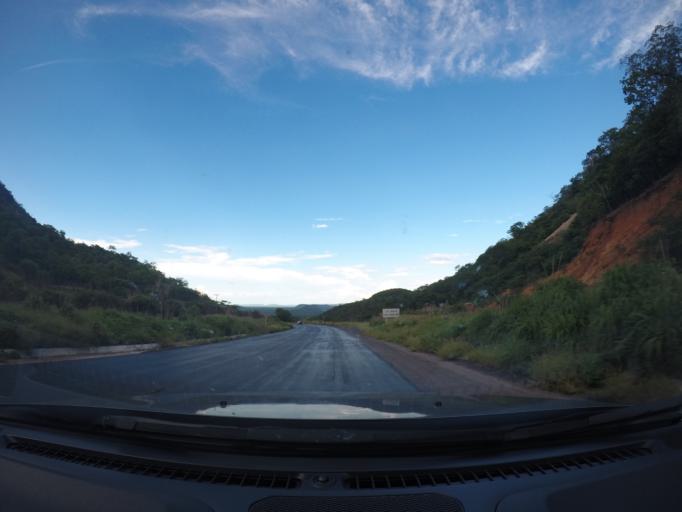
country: BR
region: Bahia
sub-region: Ibotirama
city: Ibotirama
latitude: -12.1402
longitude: -43.3521
